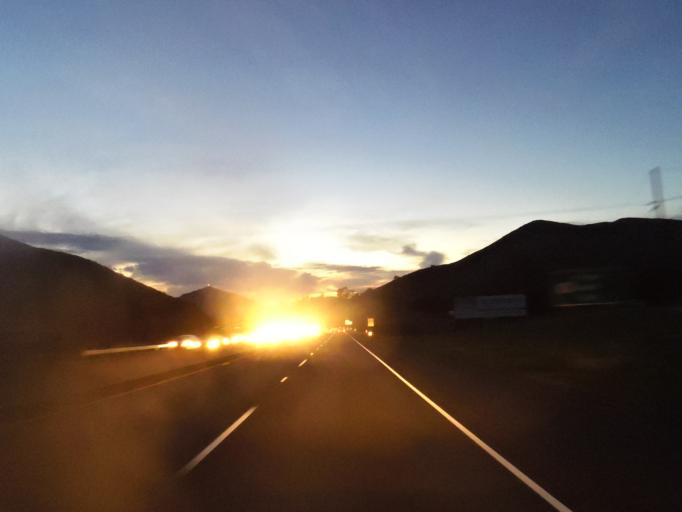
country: US
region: California
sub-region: San Luis Obispo County
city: San Luis Obispo
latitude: 35.2953
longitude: -120.6353
